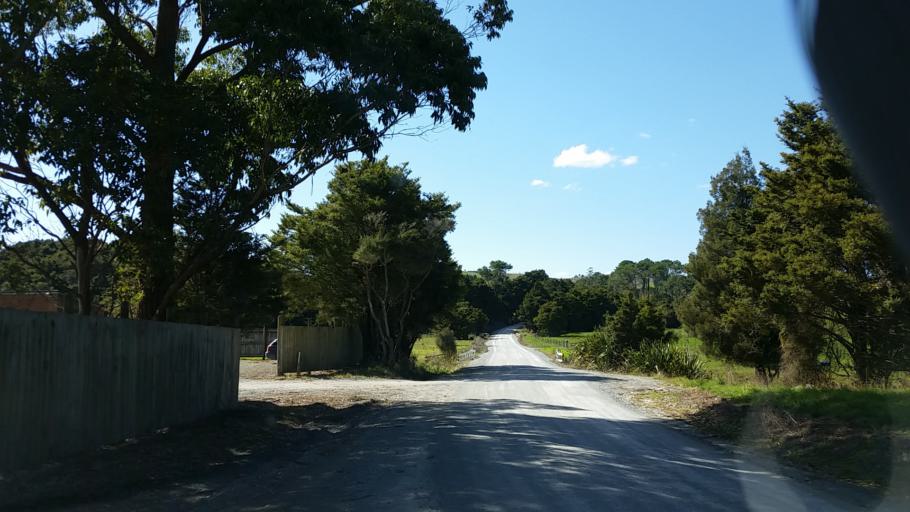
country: NZ
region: Northland
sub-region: Whangarei
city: Maungatapere
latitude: -35.6955
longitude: 174.2126
